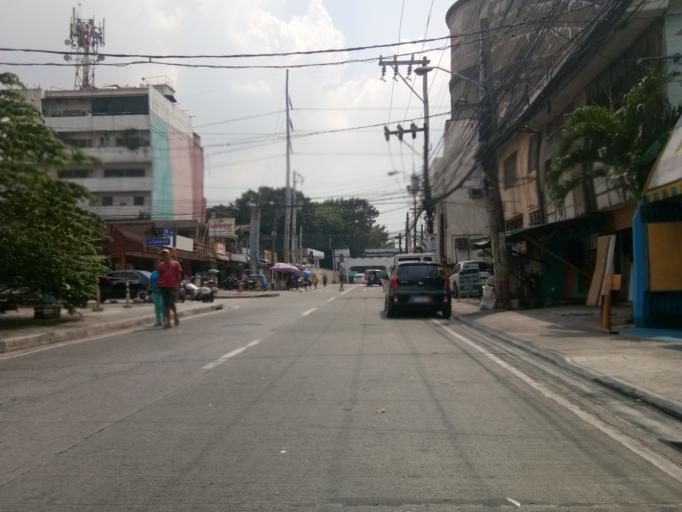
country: PH
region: Metro Manila
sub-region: Pasig
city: Pasig City
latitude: 14.6134
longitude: 121.0624
